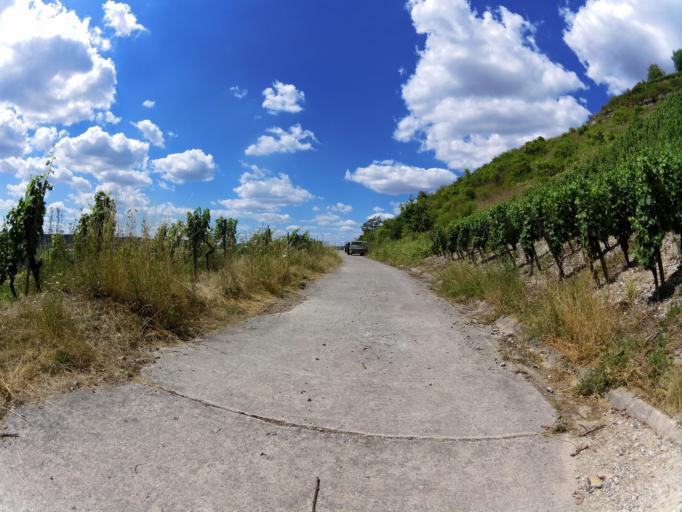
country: DE
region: Bavaria
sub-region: Regierungsbezirk Unterfranken
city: Thungersheim
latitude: 49.8929
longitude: 9.8405
